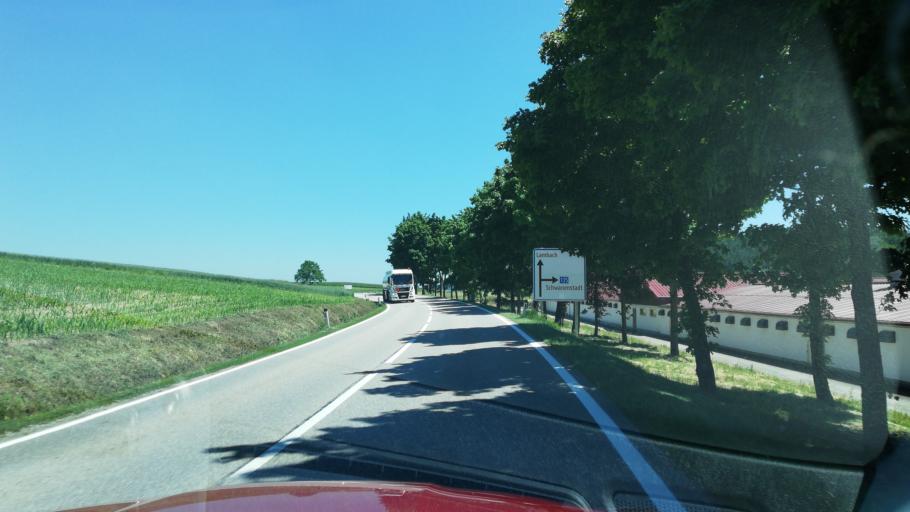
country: AT
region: Upper Austria
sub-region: Politischer Bezirk Vocklabruck
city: Niederthalheim
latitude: 48.1303
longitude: 13.7399
